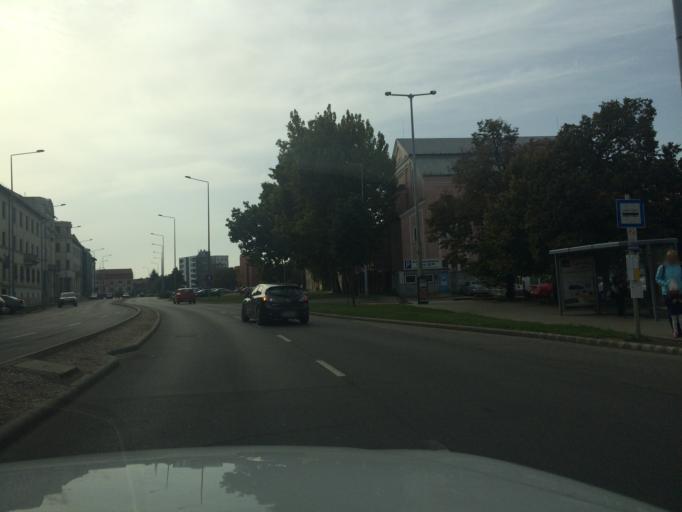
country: HU
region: Szabolcs-Szatmar-Bereg
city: Nyiregyhaza
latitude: 47.9582
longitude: 21.7134
